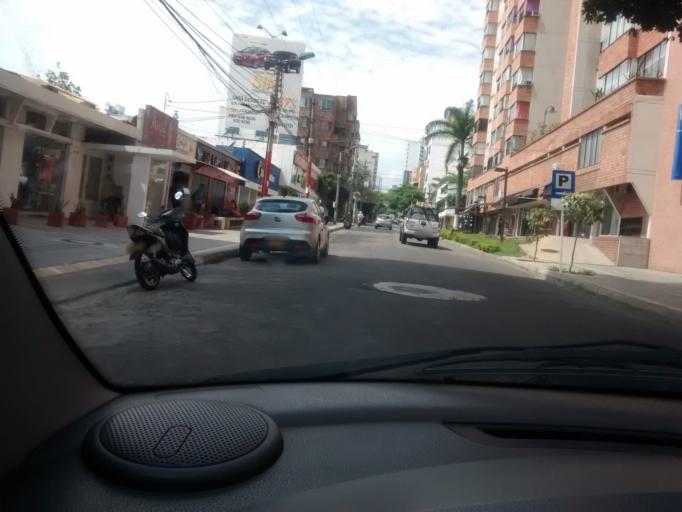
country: CO
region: Santander
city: Bucaramanga
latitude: 7.1162
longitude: -73.1086
